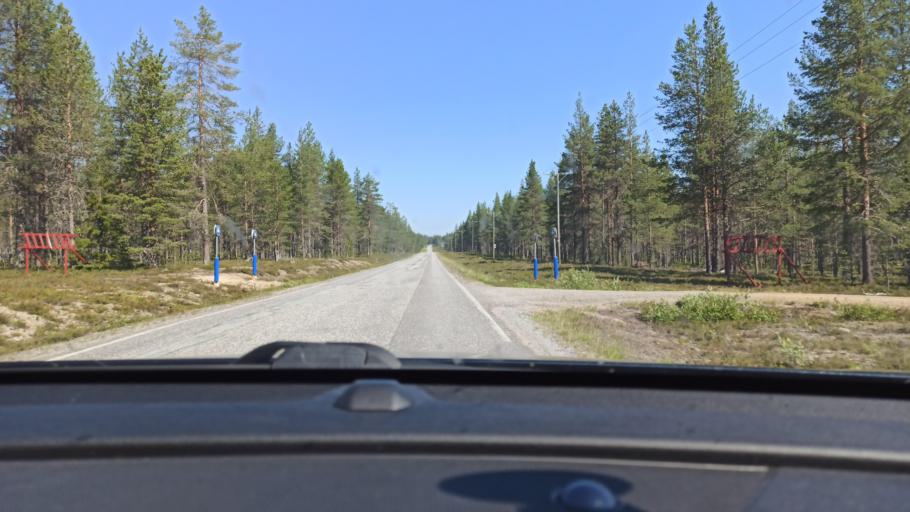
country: FI
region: Lapland
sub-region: Tunturi-Lappi
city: Kolari
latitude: 67.6469
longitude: 24.1605
